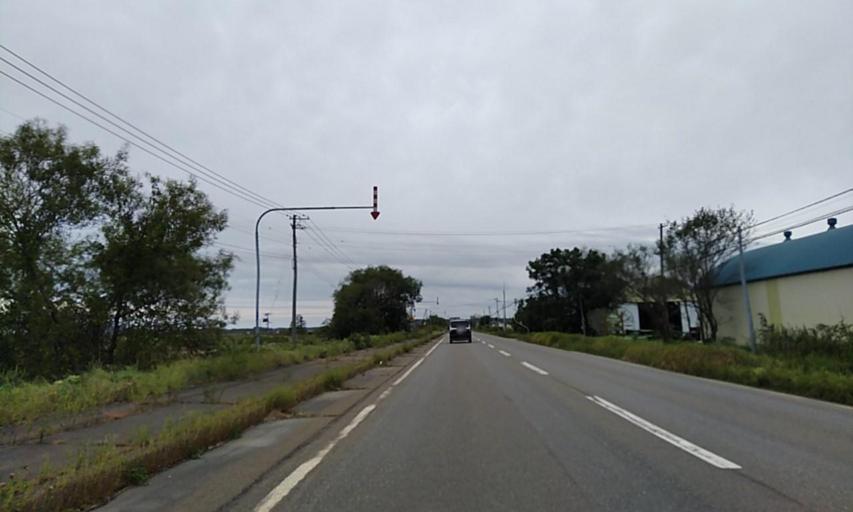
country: JP
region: Hokkaido
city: Obihiro
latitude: 42.4774
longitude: 143.2737
